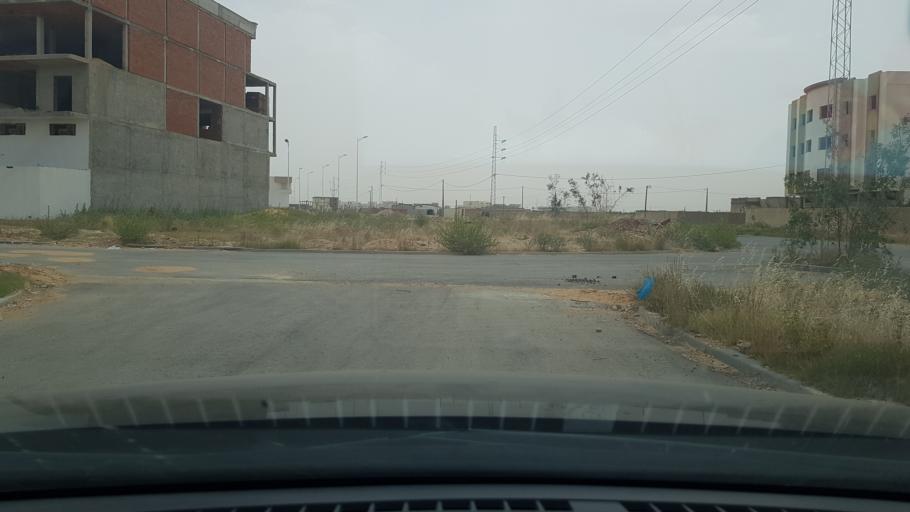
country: TN
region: Safaqis
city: Al Qarmadah
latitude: 34.8283
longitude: 10.7400
